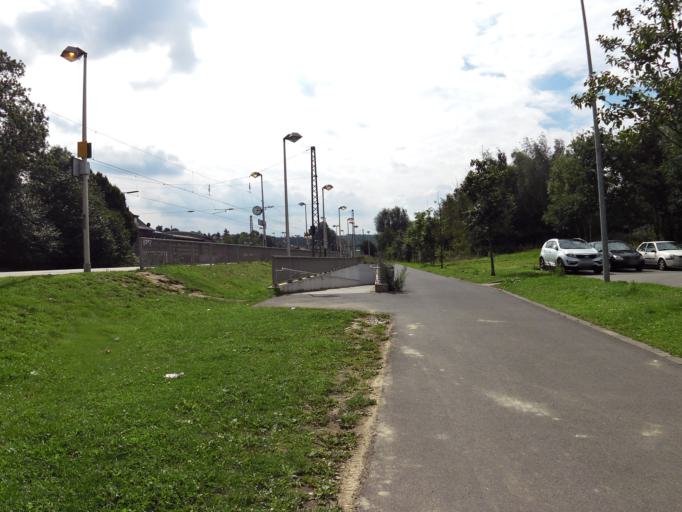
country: DE
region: North Rhine-Westphalia
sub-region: Regierungsbezirk Koln
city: Ubach-Palenberg
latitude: 50.9251
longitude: 6.0973
